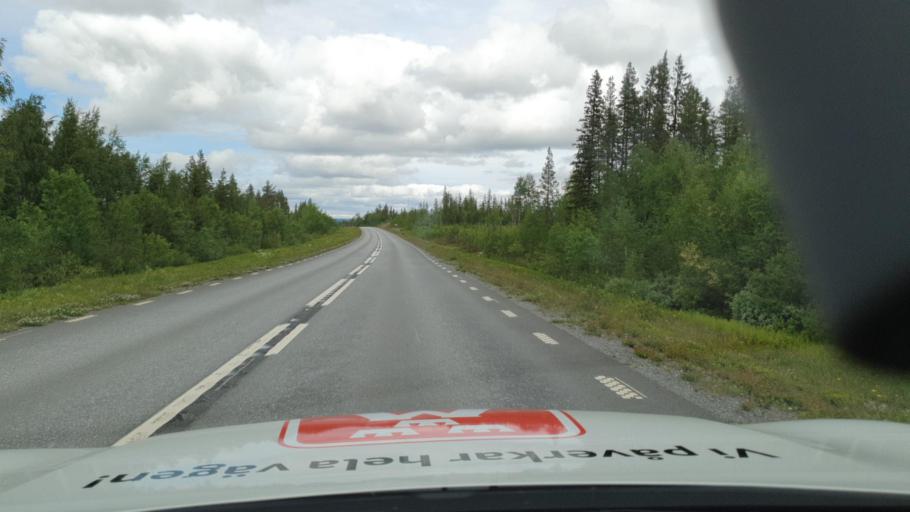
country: SE
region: Vaesterbotten
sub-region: Vilhelmina Kommun
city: Vilhelmina
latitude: 64.4058
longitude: 16.7321
